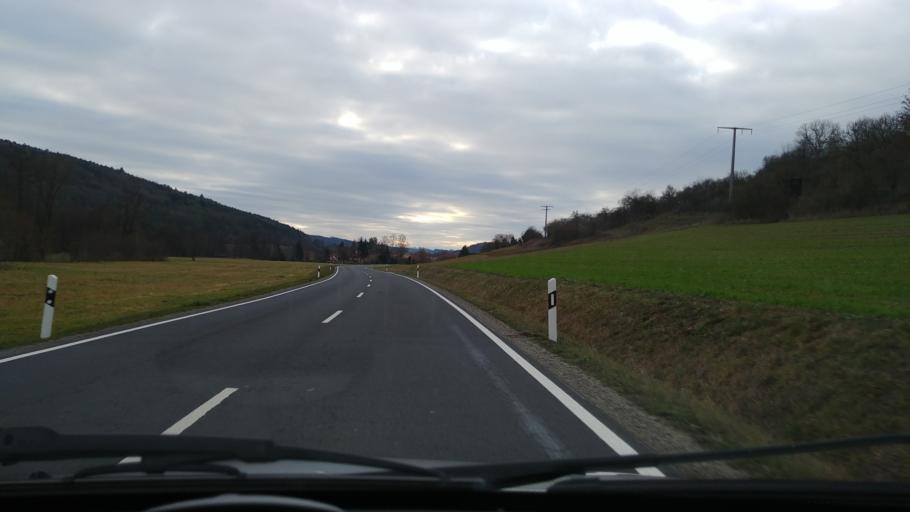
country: DE
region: Bavaria
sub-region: Regierungsbezirk Unterfranken
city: Thungen
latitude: 49.9644
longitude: 9.9054
